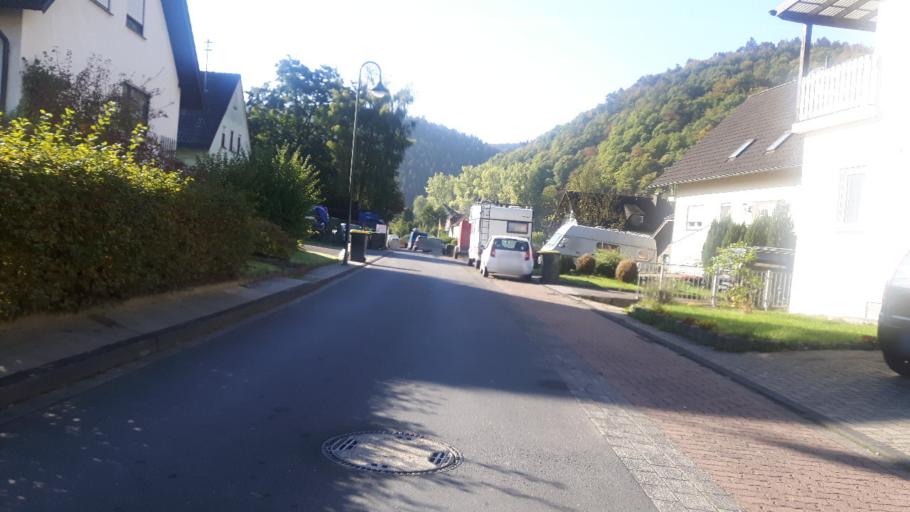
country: DE
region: Rheinland-Pfalz
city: Niederirsen
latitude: 50.8007
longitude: 7.5582
